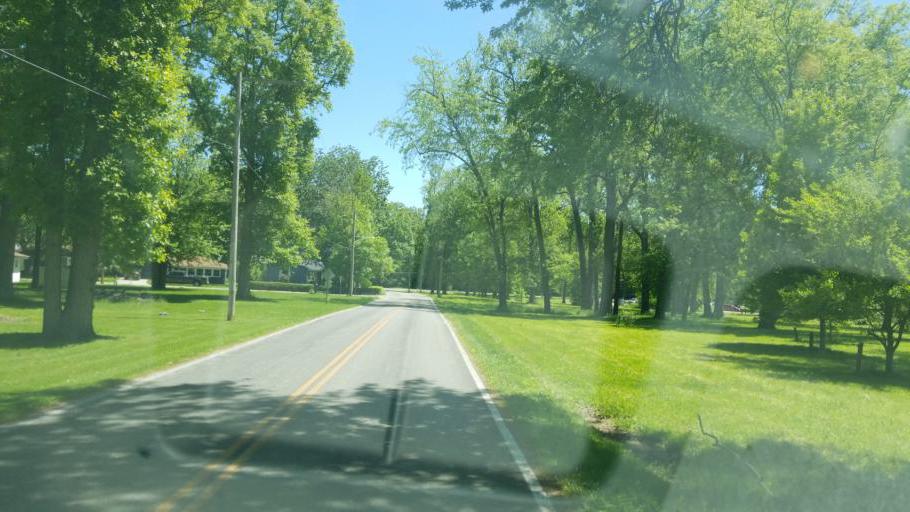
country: US
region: Ohio
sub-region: Shelby County
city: Fort Loramie
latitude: 40.3697
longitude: -84.3406
